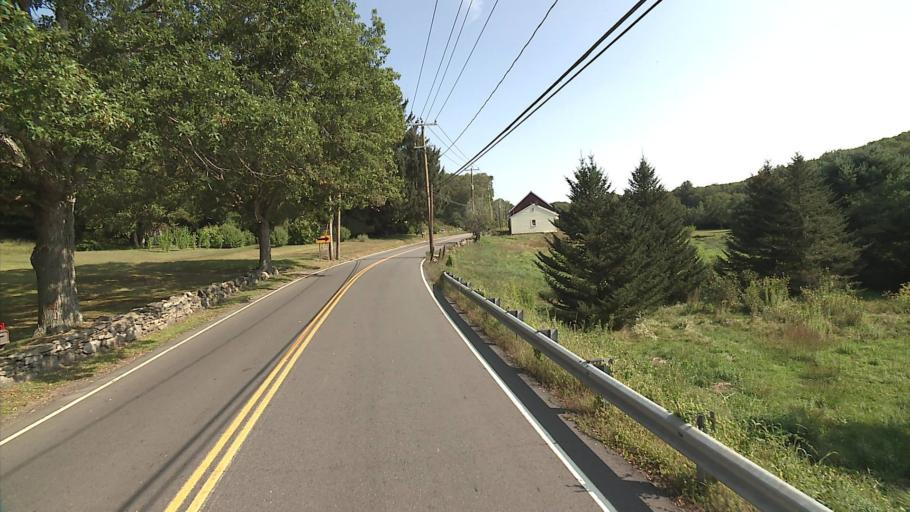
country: US
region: Connecticut
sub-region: New London County
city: Lisbon
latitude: 41.5772
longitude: -72.0297
